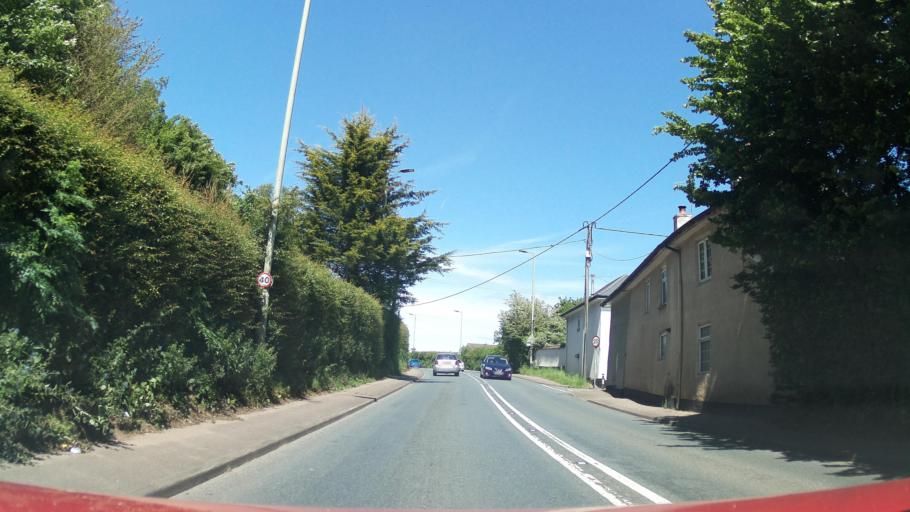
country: GB
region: England
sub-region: Devon
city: Topsham
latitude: 50.6837
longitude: -3.4441
